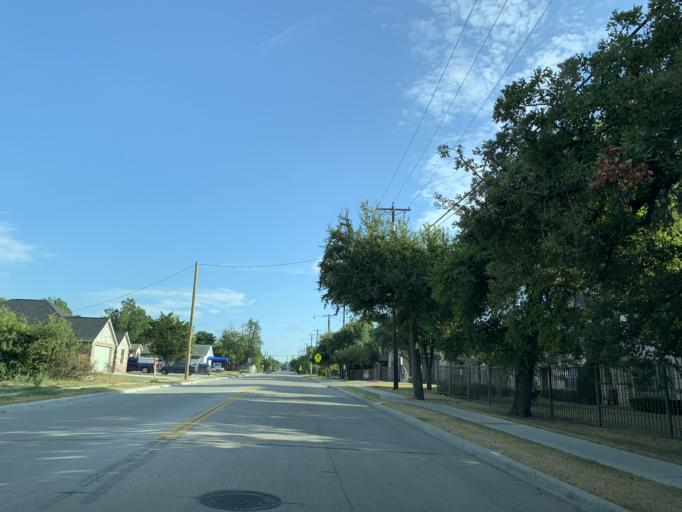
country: US
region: Texas
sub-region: Dallas County
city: Dallas
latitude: 32.7350
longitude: -96.8115
